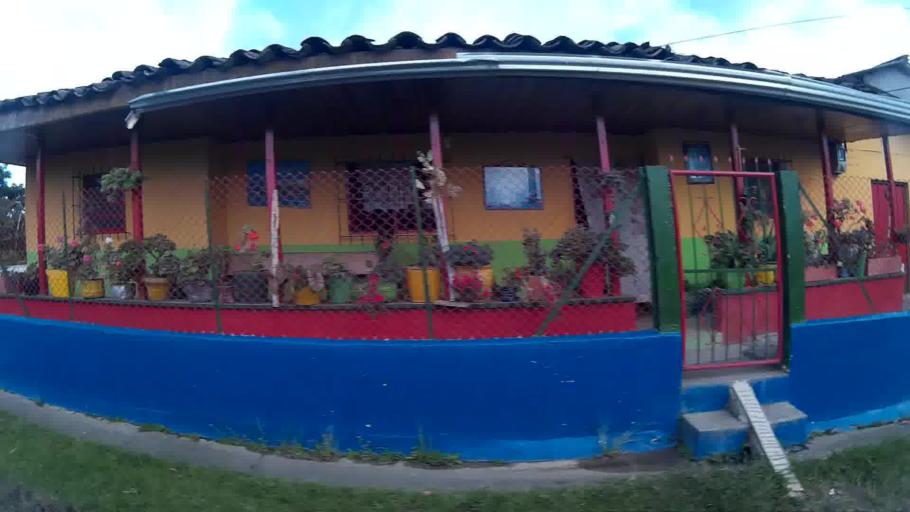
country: CO
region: Valle del Cauca
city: Ulloa
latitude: 4.7205
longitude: -75.7063
